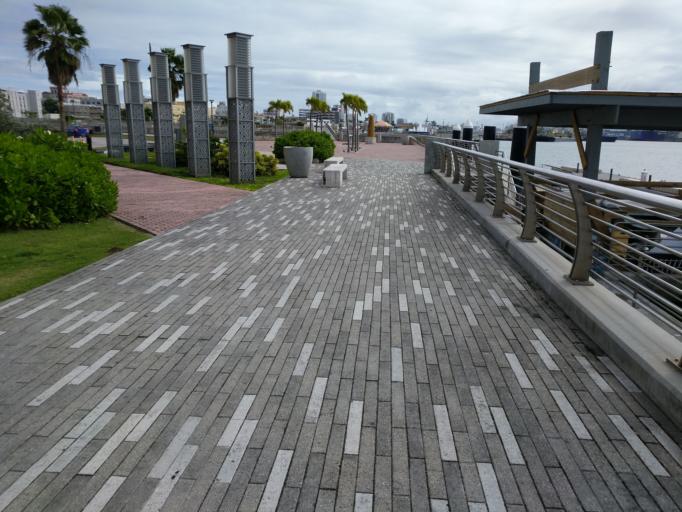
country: PR
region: San Juan
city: San Juan
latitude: 18.4635
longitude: -66.1076
